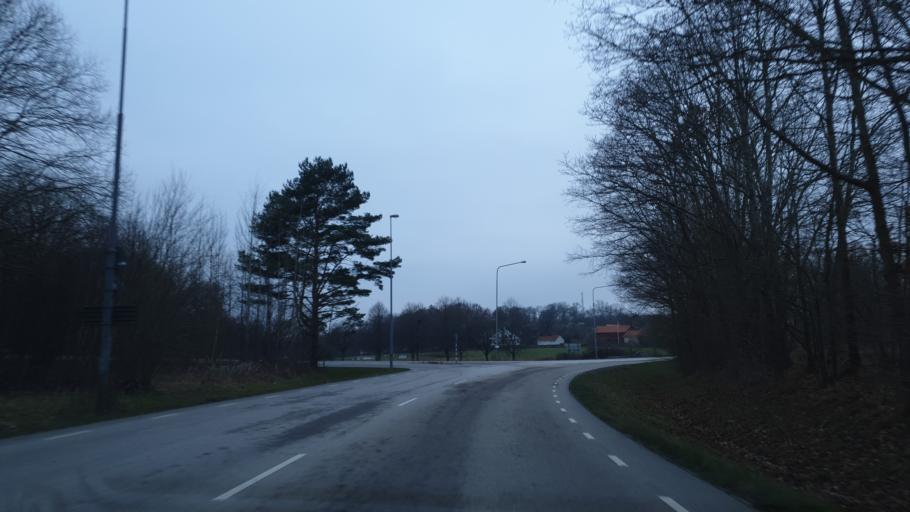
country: SE
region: Blekinge
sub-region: Karlskrona Kommun
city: Rodeby
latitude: 56.2074
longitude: 15.6617
